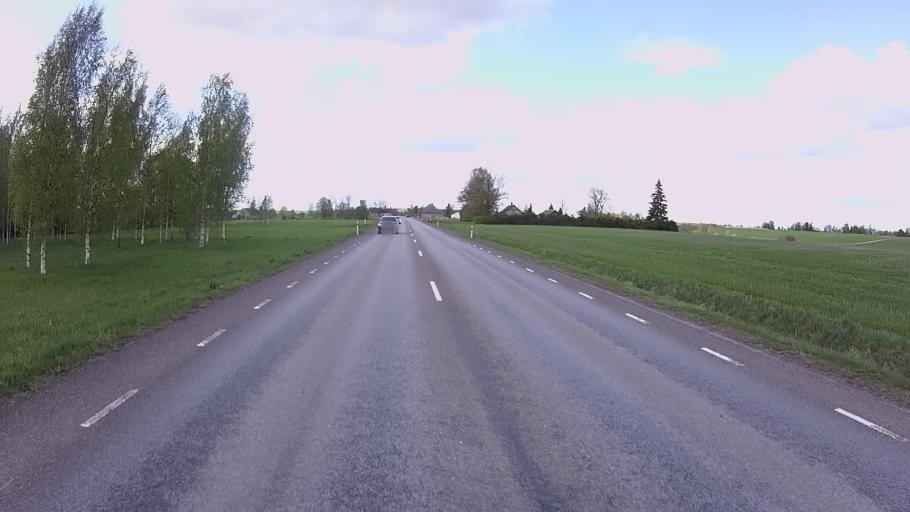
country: EE
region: Jogevamaa
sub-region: Tabivere vald
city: Tabivere
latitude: 58.5171
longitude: 26.6624
